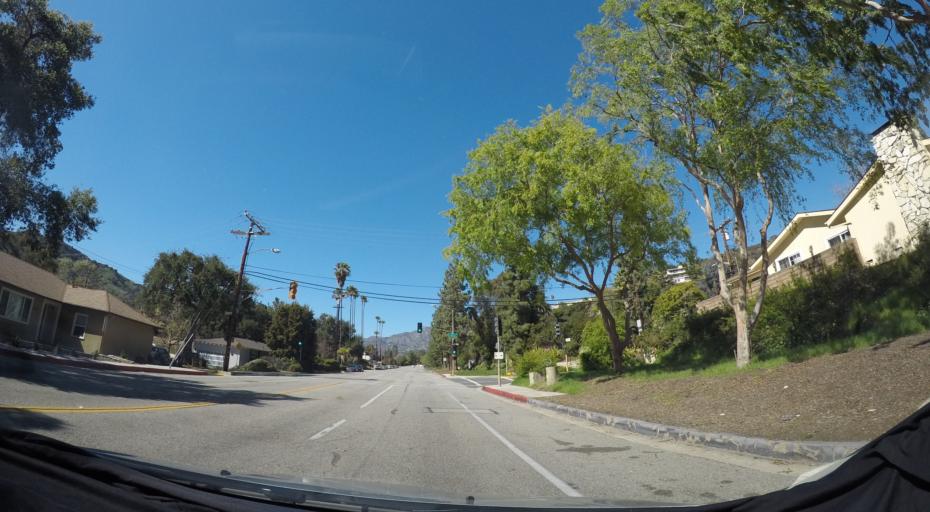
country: US
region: California
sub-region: Los Angeles County
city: La Canada Flintridge
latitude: 34.1821
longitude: -118.2257
